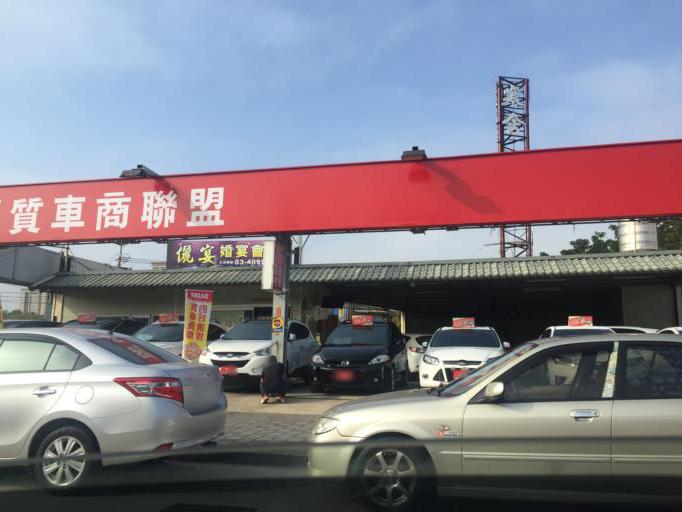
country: TW
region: Taiwan
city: Daxi
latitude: 24.8656
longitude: 121.2223
